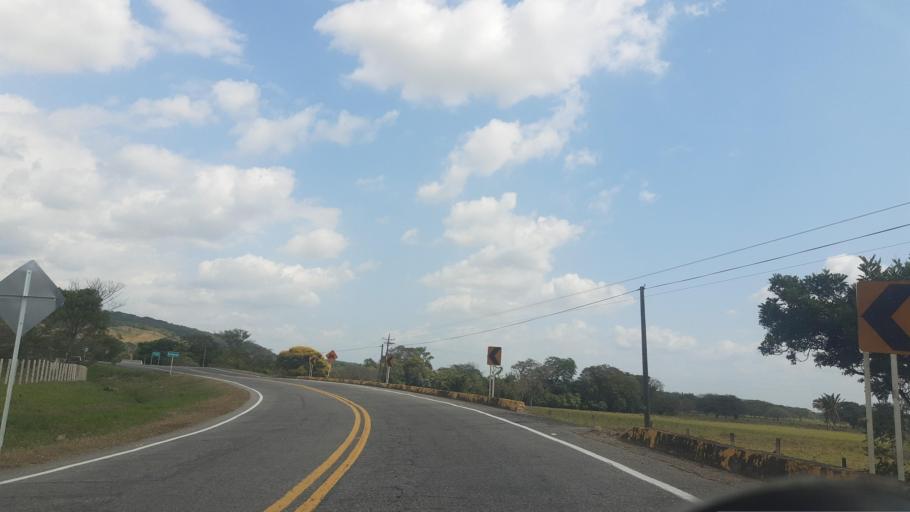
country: CO
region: Casanare
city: Tauramena
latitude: 4.8693
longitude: -72.7055
